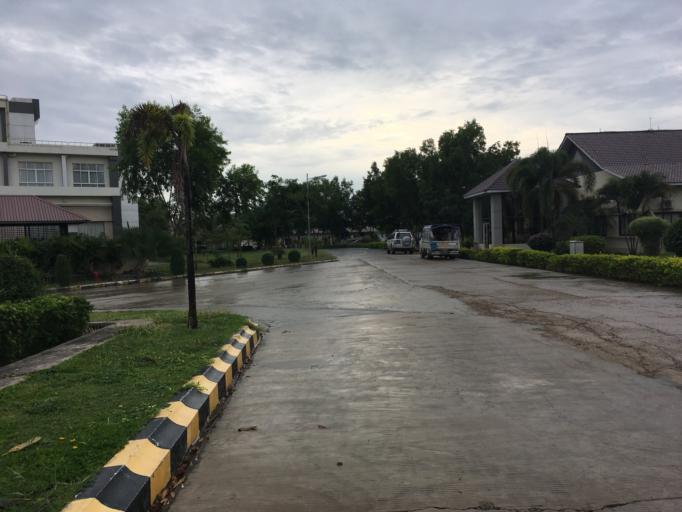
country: MM
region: Mandalay
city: Nay Pyi Taw
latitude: 19.7014
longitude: 96.1177
